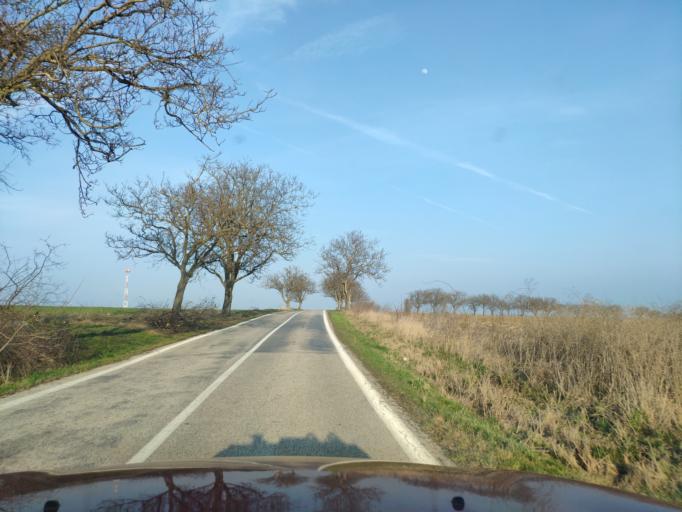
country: SK
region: Bratislavsky
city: Modra
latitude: 48.3296
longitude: 17.4121
